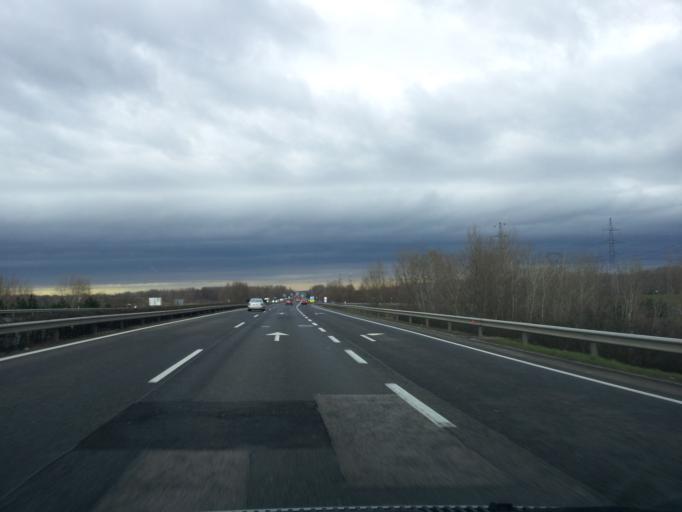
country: HU
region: Gyor-Moson-Sopron
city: Gyor
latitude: 47.6442
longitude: 17.6186
